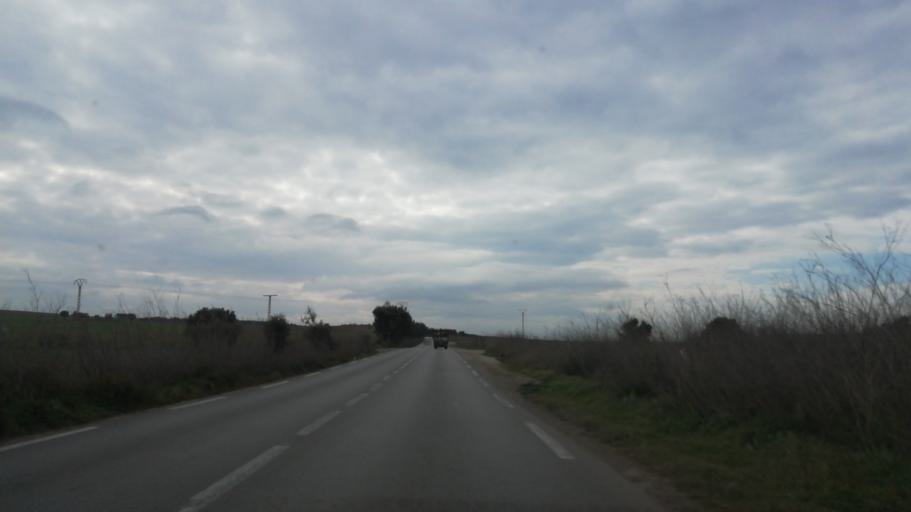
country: DZ
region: Oran
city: Ain el Bya
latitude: 35.7572
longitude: -0.3506
